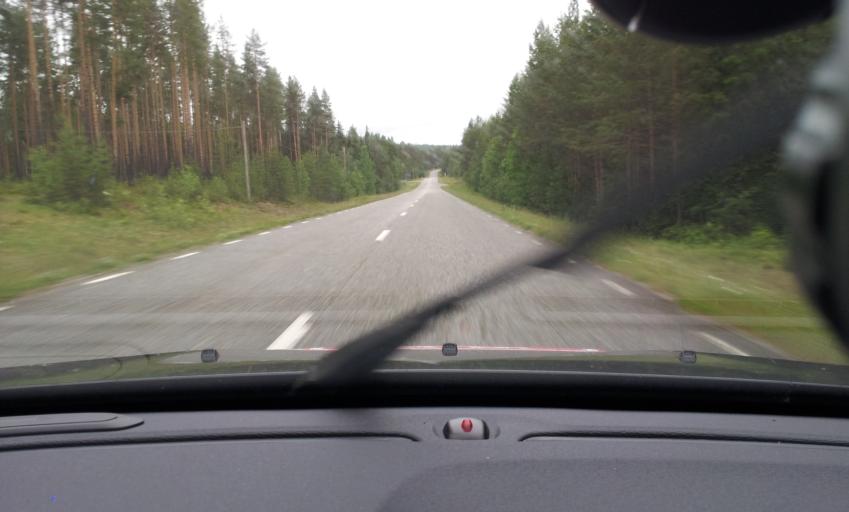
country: SE
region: Jaemtland
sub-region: Ragunda Kommun
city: Hammarstrand
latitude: 63.2561
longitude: 15.8997
